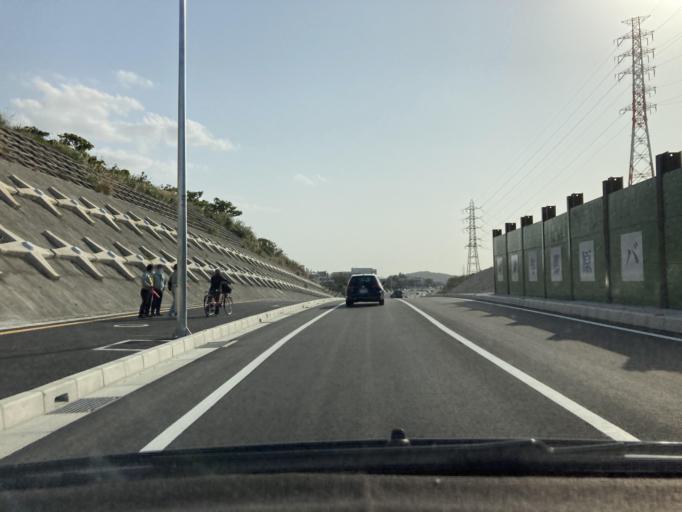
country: JP
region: Okinawa
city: Ginowan
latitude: 26.2059
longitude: 127.7504
